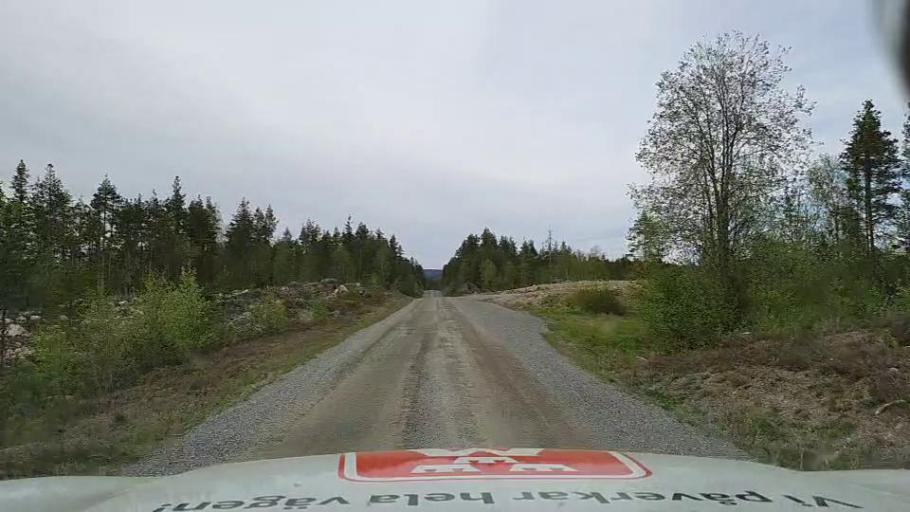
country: SE
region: Jaemtland
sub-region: Braecke Kommun
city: Braecke
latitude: 62.4740
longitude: 14.9164
